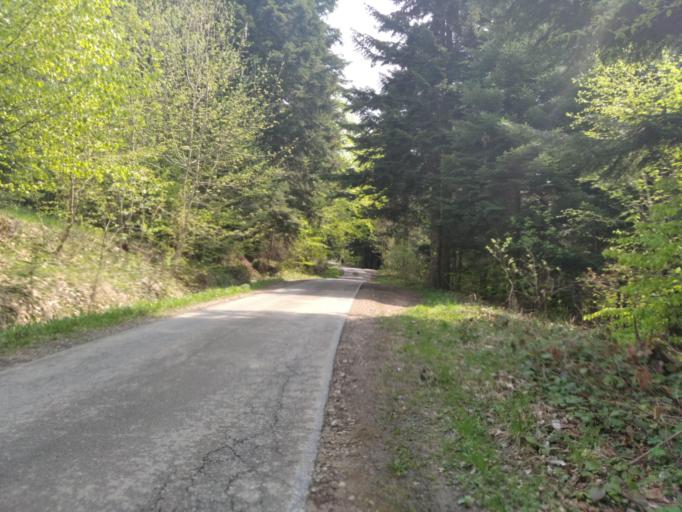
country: PL
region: Subcarpathian Voivodeship
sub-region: Powiat krosnienski
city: Iwonicz-Zdroj
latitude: 49.5430
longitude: 21.7880
